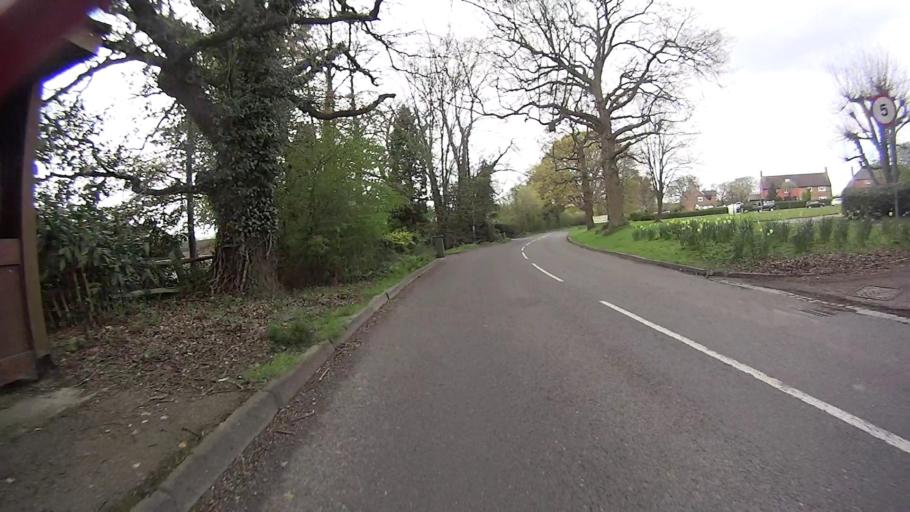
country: GB
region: England
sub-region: Surrey
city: Newdigate
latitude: 51.1174
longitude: -0.2840
